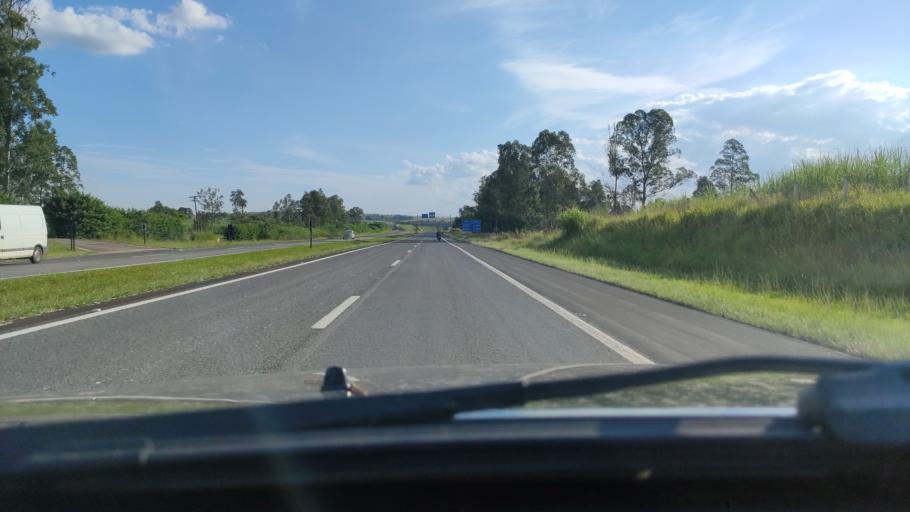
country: BR
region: Sao Paulo
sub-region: Mogi-Mirim
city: Mogi Mirim
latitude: -22.4517
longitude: -46.8910
